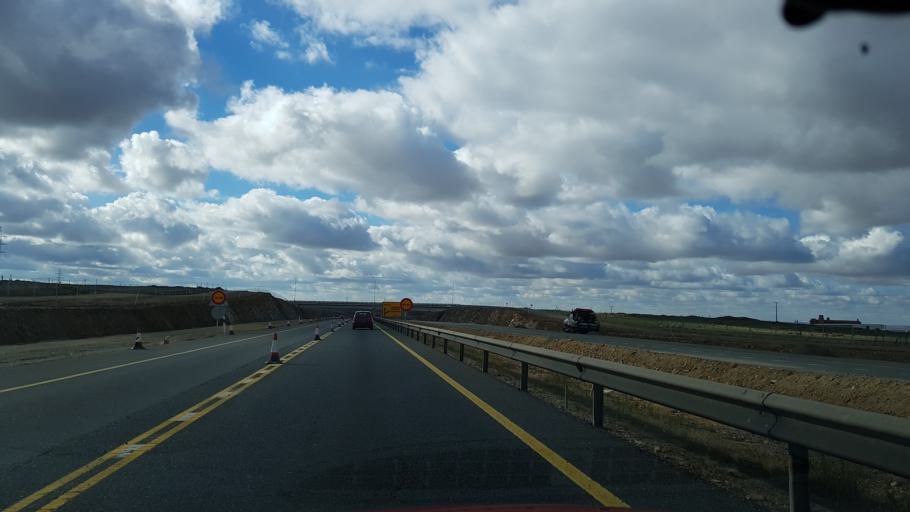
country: ES
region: Castille and Leon
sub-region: Provincia de Segovia
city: Segovia
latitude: 40.9216
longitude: -4.0978
